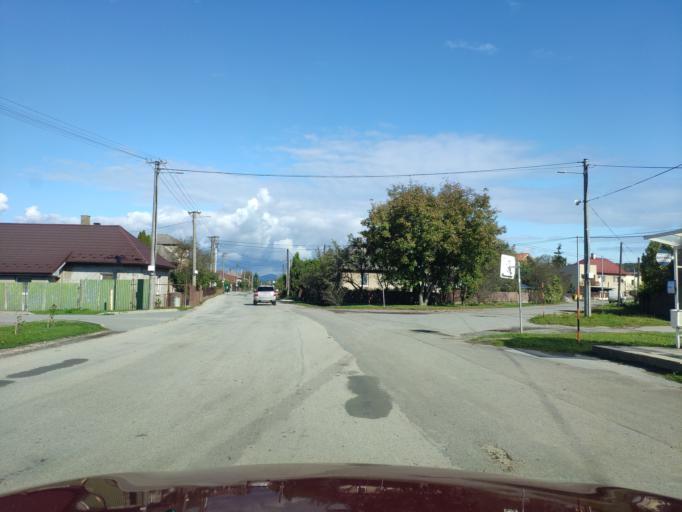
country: SK
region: Presovsky
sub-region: Okres Presov
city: Presov
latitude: 48.9228
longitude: 21.2605
